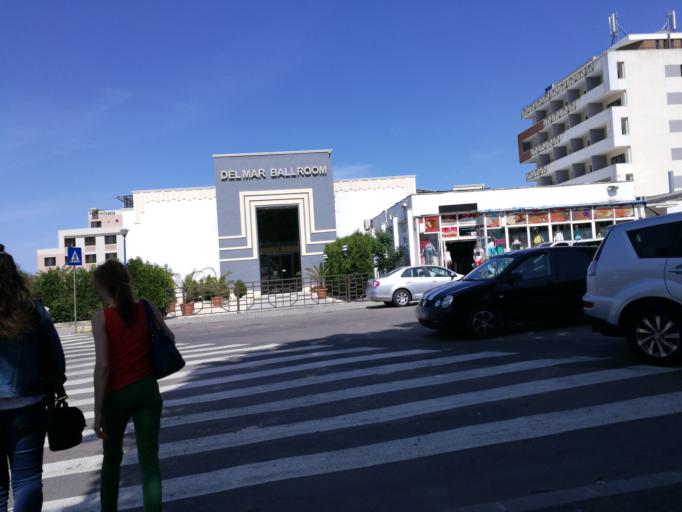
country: RO
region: Constanta
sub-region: Municipiul Constanta
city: Palazu Mare
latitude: 44.2197
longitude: 28.6324
